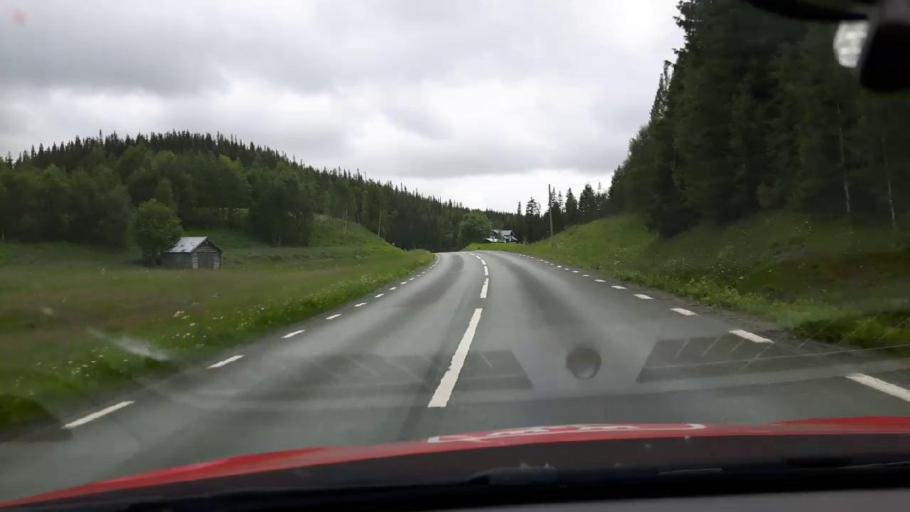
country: SE
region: Jaemtland
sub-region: Are Kommun
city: Are
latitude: 63.3843
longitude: 12.7625
